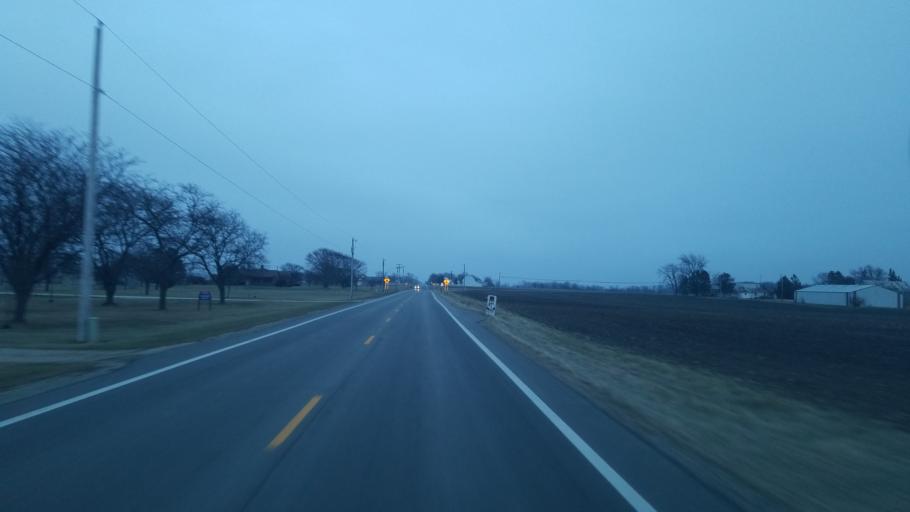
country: US
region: Ohio
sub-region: Mercer County
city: Rockford
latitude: 40.6550
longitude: -84.6517
